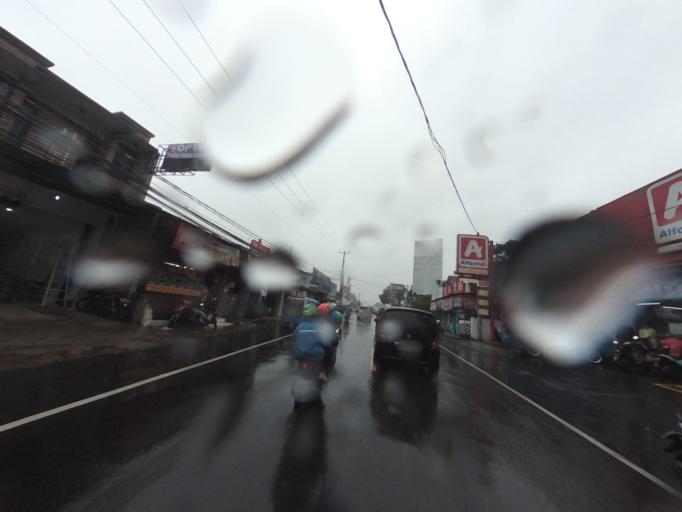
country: ID
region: West Java
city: Caringin
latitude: -6.6550
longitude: 106.8611
